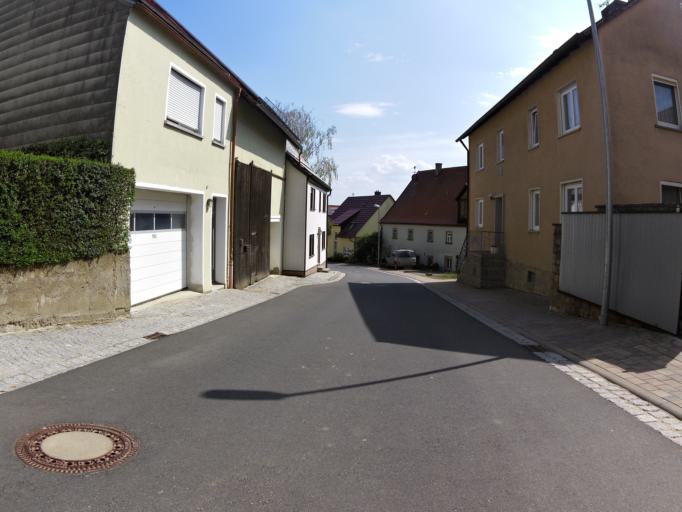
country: DE
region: Bavaria
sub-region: Regierungsbezirk Unterfranken
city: Giebelstadt
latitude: 49.6730
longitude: 9.9600
